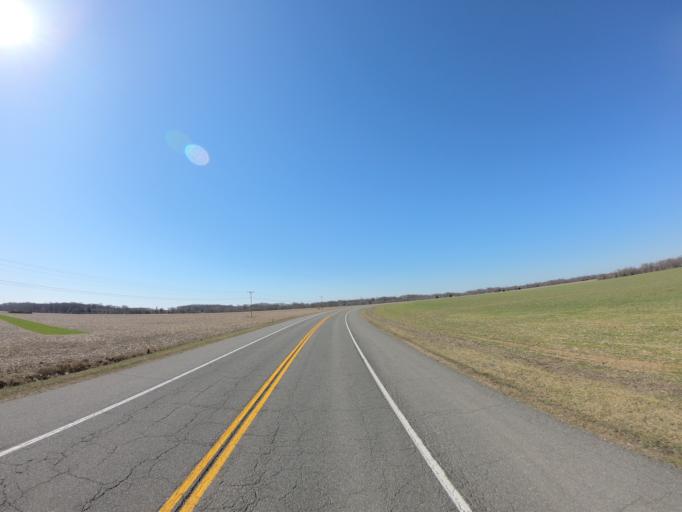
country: US
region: Delaware
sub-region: New Castle County
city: Townsend
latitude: 39.3441
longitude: -75.8454
